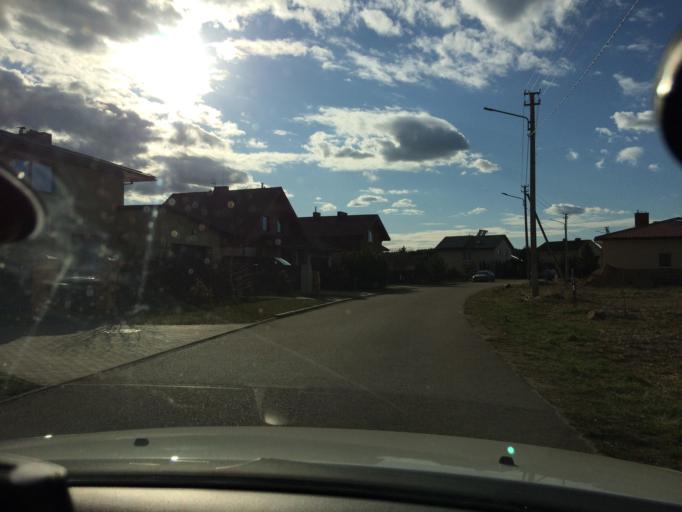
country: LT
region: Vilnius County
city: Rasos
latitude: 54.7758
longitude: 25.3497
